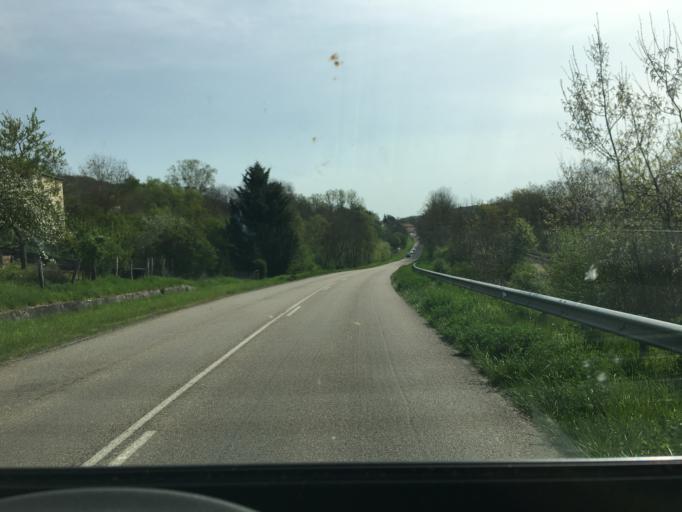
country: FR
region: Lorraine
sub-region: Departement de Meurthe-et-Moselle
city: Messein
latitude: 48.6112
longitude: 6.1344
